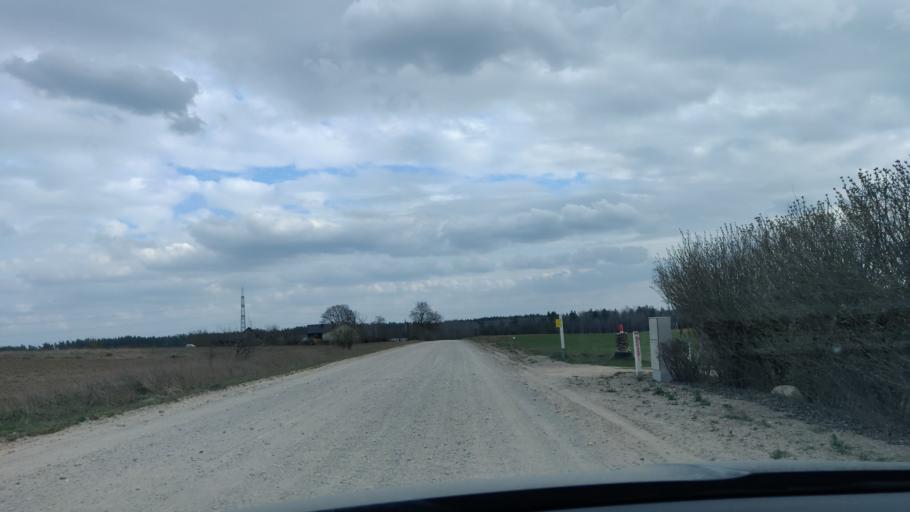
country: LT
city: Lentvaris
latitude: 54.6120
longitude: 25.0702
